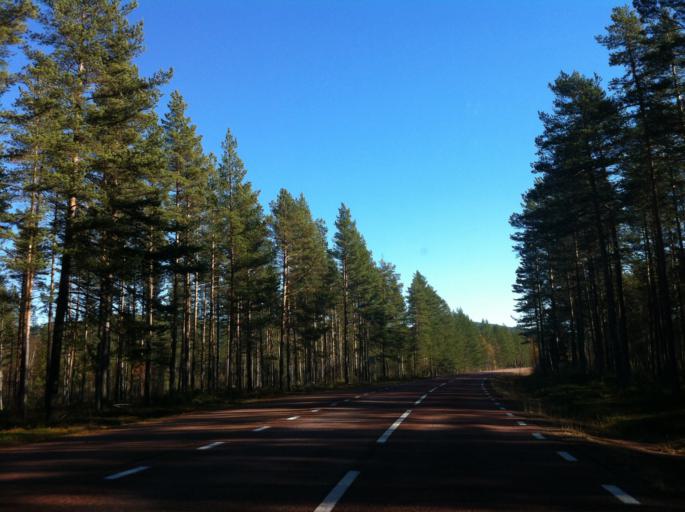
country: SE
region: Dalarna
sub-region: Alvdalens Kommun
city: AElvdalen
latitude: 61.3141
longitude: 13.6747
